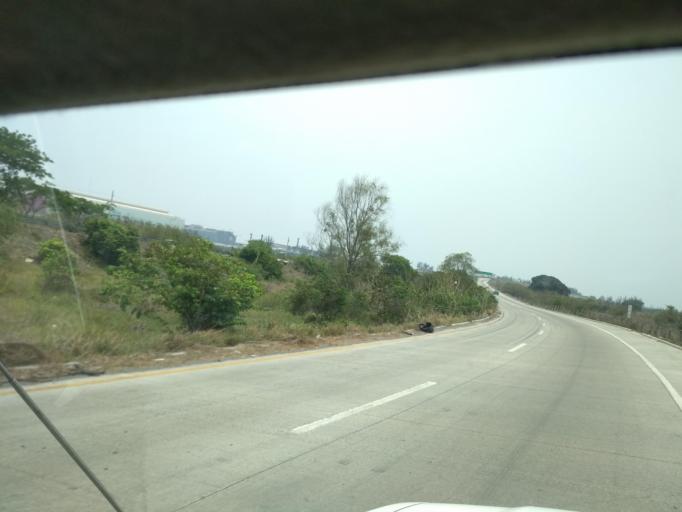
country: MX
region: Veracruz
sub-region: Veracruz
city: Oasis
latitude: 19.1900
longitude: -96.2460
